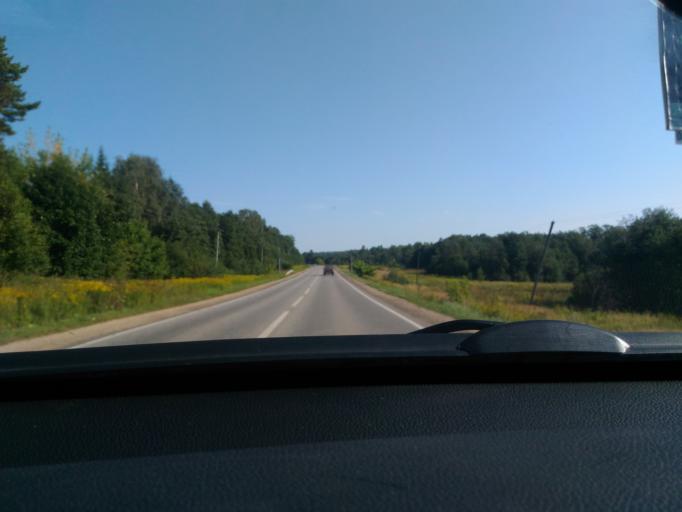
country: RU
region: Moskovskaya
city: Podosinki
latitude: 56.2161
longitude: 37.5456
